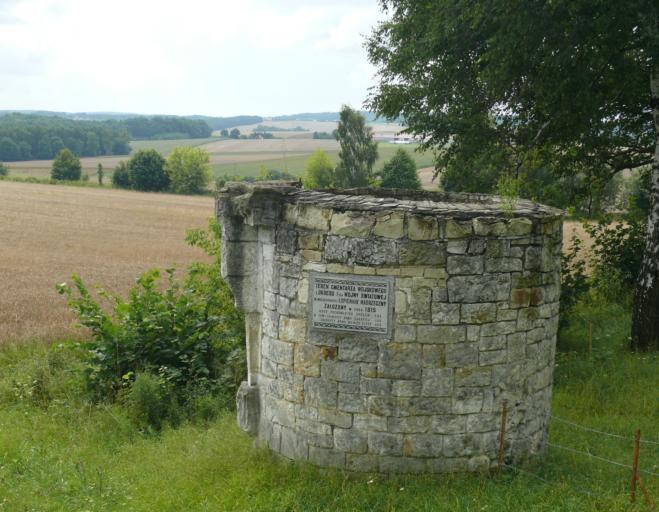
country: PL
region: Lublin Voivodeship
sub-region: Powiat krasnostawski
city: Lopiennik Gorny
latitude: 51.0255
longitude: 23.0801
